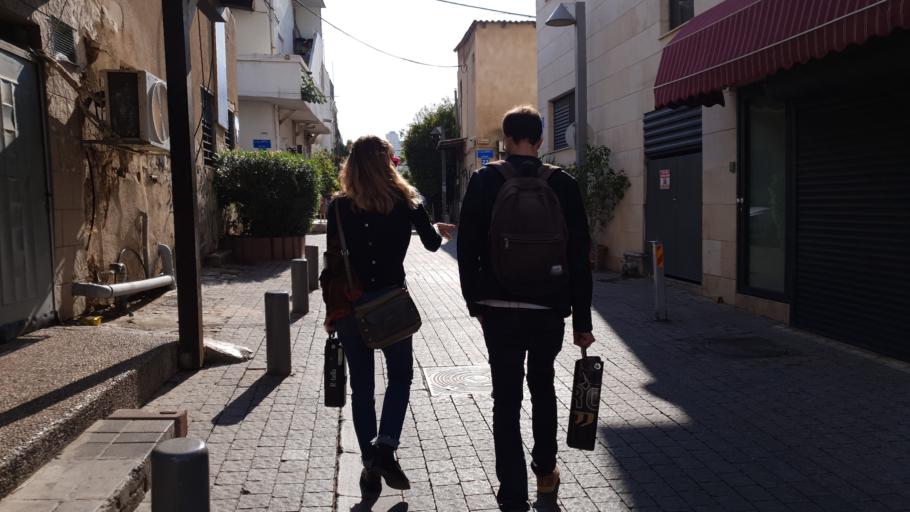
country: IL
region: Tel Aviv
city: Tel Aviv
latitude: 32.0689
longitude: 34.7673
